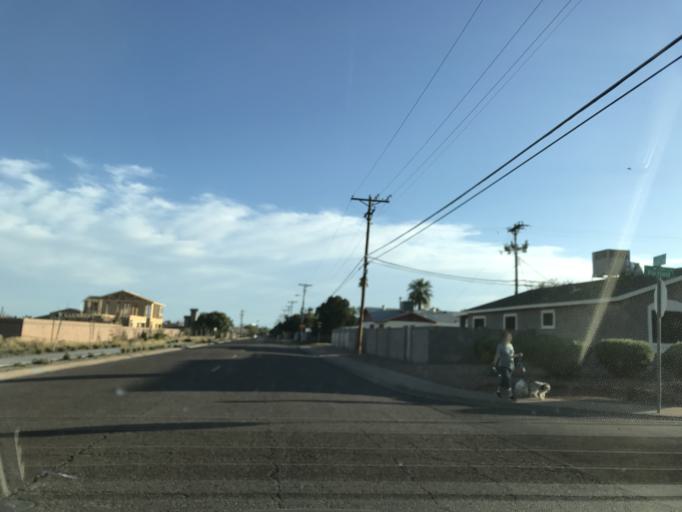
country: US
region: Arizona
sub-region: Maricopa County
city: Tempe Junction
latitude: 33.4600
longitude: -111.9307
